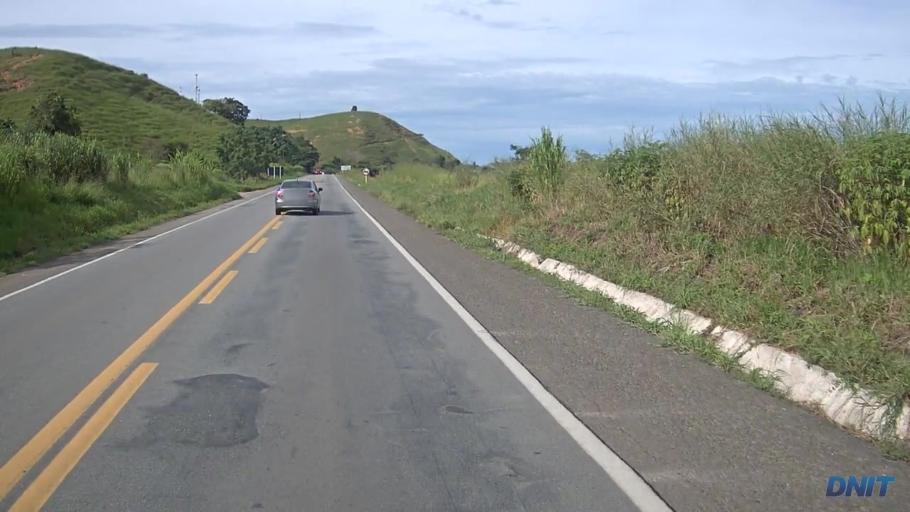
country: BR
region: Minas Gerais
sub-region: Belo Oriente
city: Belo Oriente
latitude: -19.1700
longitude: -42.2479
